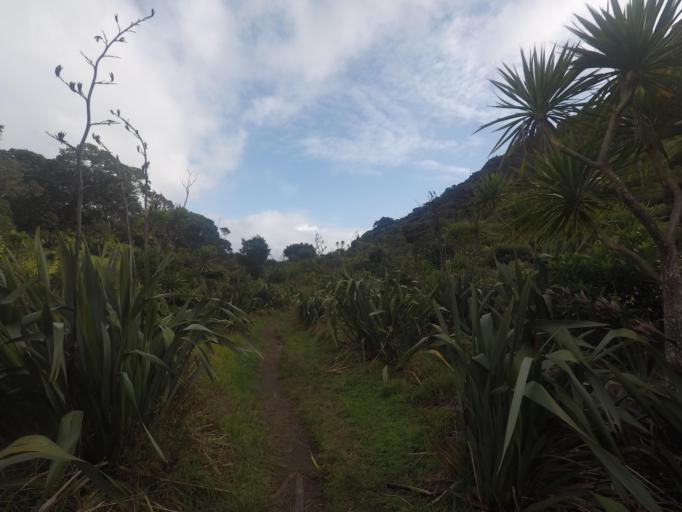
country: NZ
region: Auckland
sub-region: Auckland
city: Muriwai Beach
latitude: -36.8876
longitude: 174.4412
